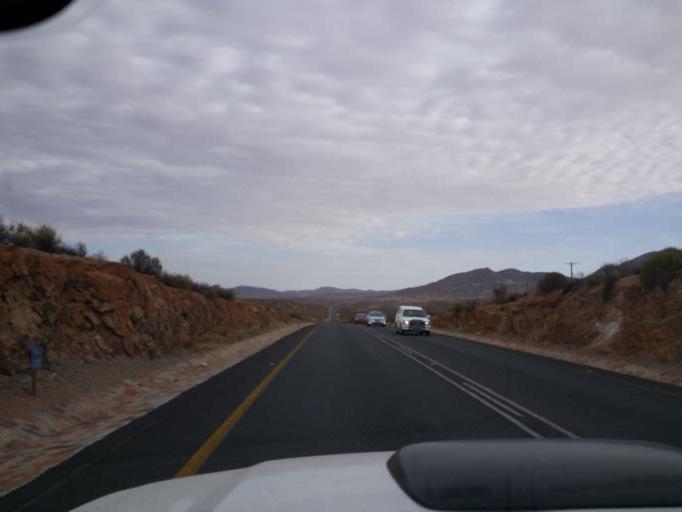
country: ZA
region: Northern Cape
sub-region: Namakwa District Municipality
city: Springbok
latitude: -29.5466
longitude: 17.8648
